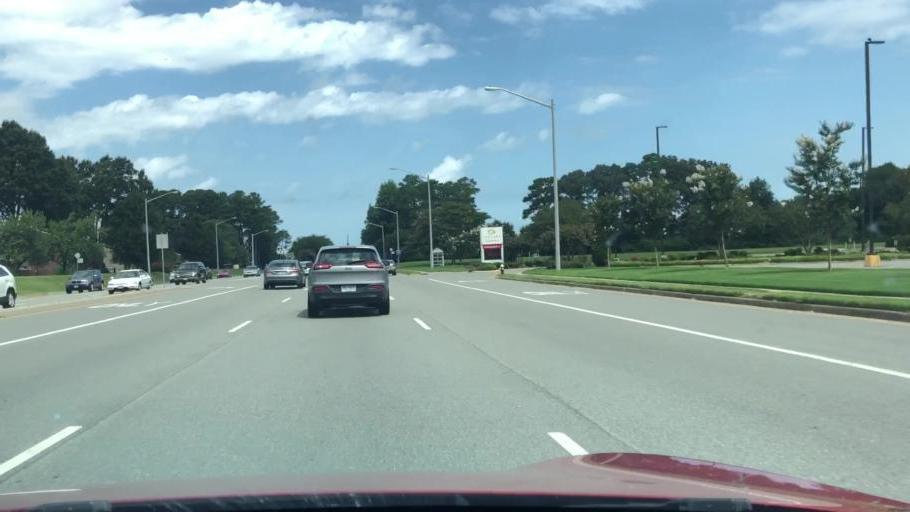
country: US
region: Virginia
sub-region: City of Chesapeake
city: Chesapeake
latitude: 36.8673
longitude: -76.1326
